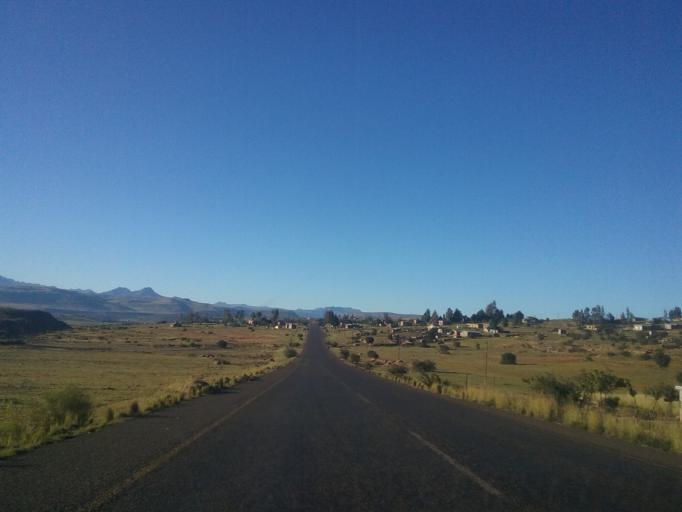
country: LS
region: Quthing
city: Quthing
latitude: -30.3585
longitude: 27.5471
